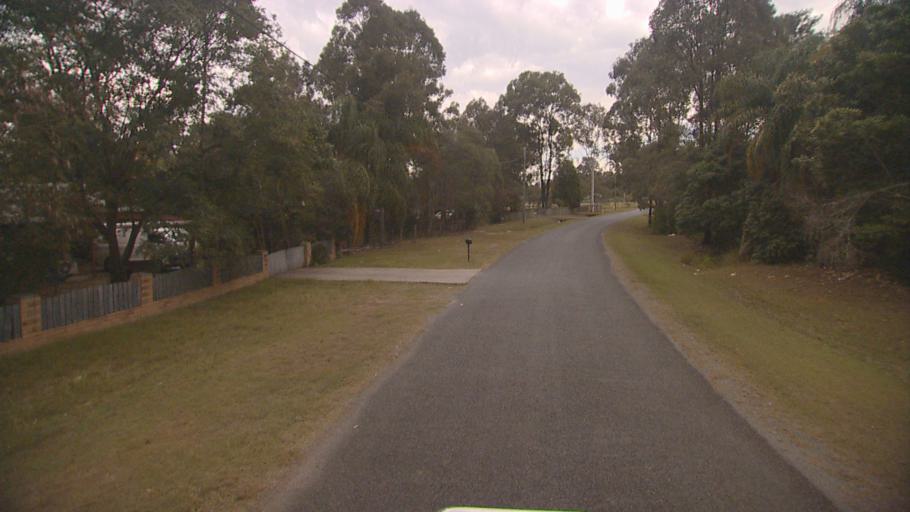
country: AU
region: Queensland
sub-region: Logan
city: Chambers Flat
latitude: -27.7884
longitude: 153.1165
